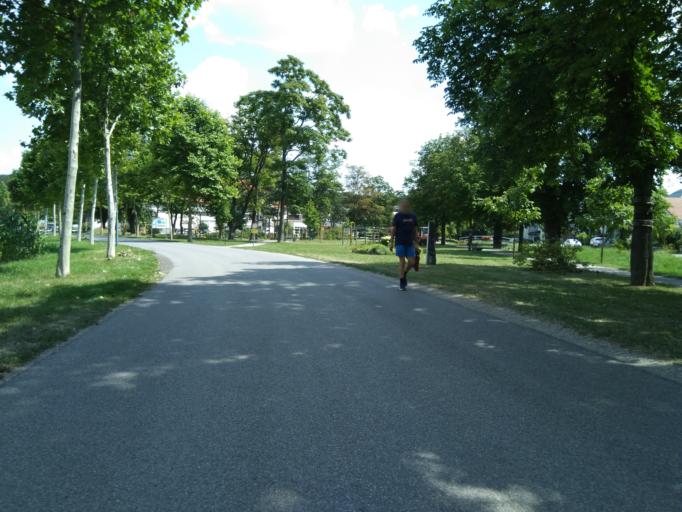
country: AT
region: Lower Austria
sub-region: Politischer Bezirk Ganserndorf
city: Bad Pirawarth
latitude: 48.4498
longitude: 16.6070
